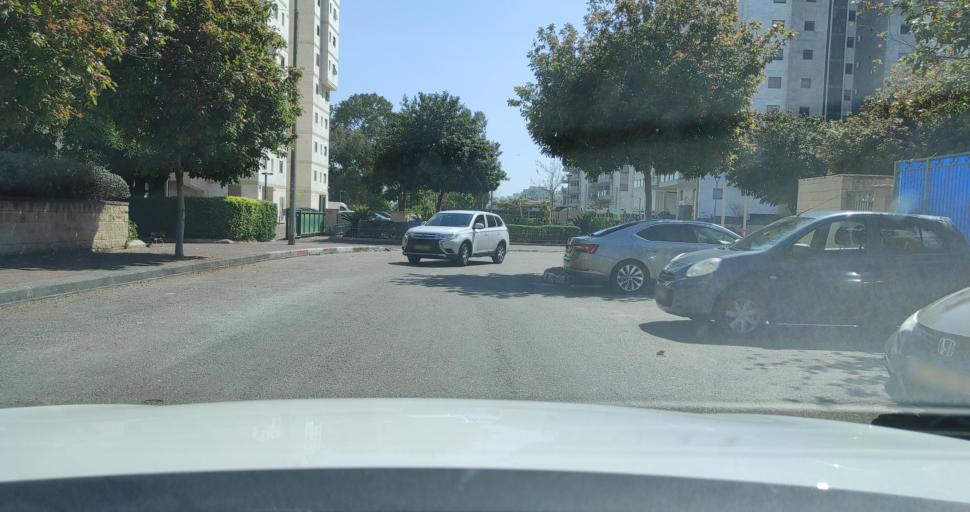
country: IL
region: Central District
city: Nordiyya
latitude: 32.3085
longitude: 34.8738
